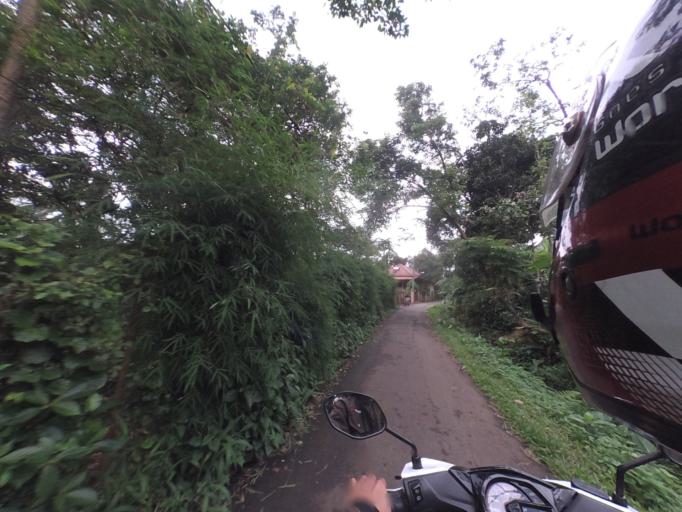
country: ID
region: West Java
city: Bogor
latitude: -6.6138
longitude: 106.7379
